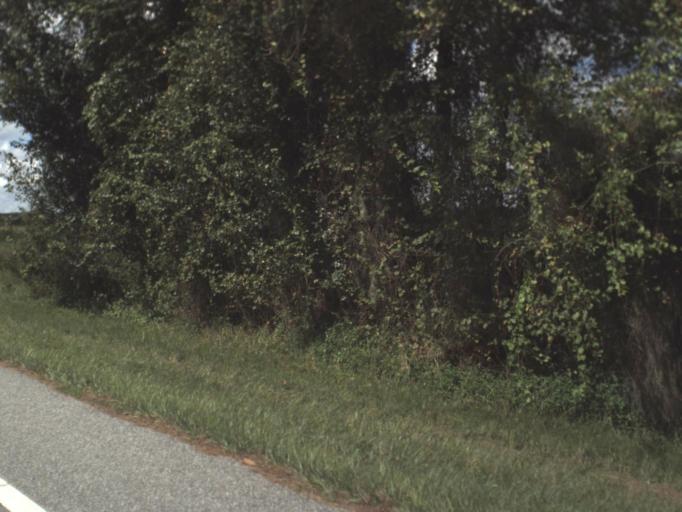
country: US
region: Florida
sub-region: DeSoto County
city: Arcadia
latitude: 27.3196
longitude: -82.1173
